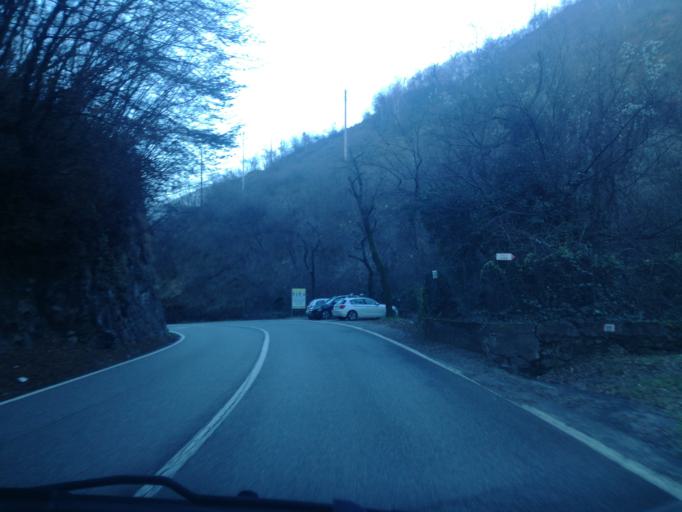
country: IT
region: Lombardy
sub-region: Provincia di Bergamo
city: Castro
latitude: 45.8067
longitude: 10.0610
